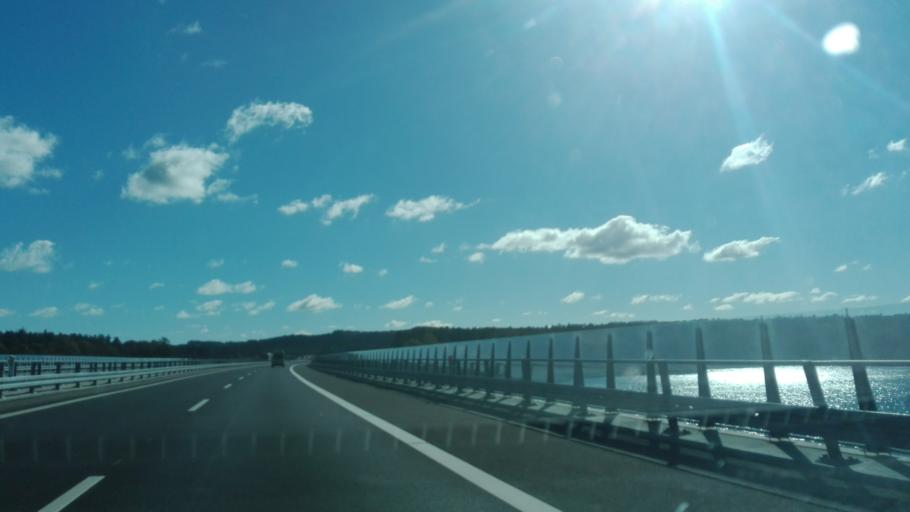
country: DK
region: Central Jutland
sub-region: Silkeborg Kommune
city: Silkeborg
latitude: 56.1753
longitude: 9.5968
